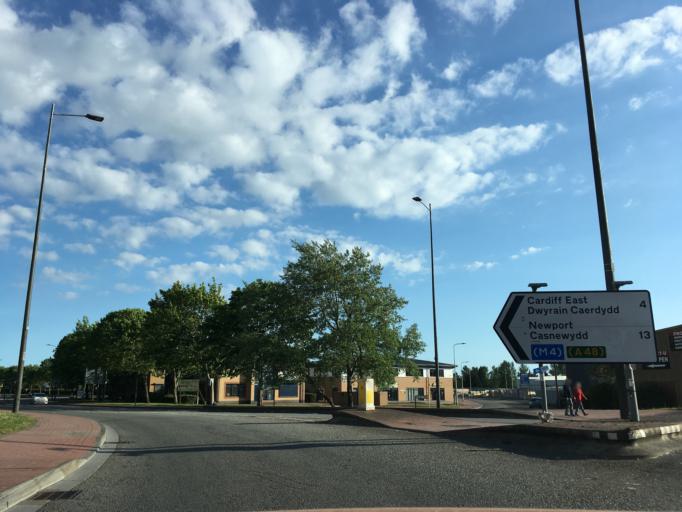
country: GB
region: Wales
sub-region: Cardiff
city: Cardiff
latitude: 51.4783
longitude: -3.1604
